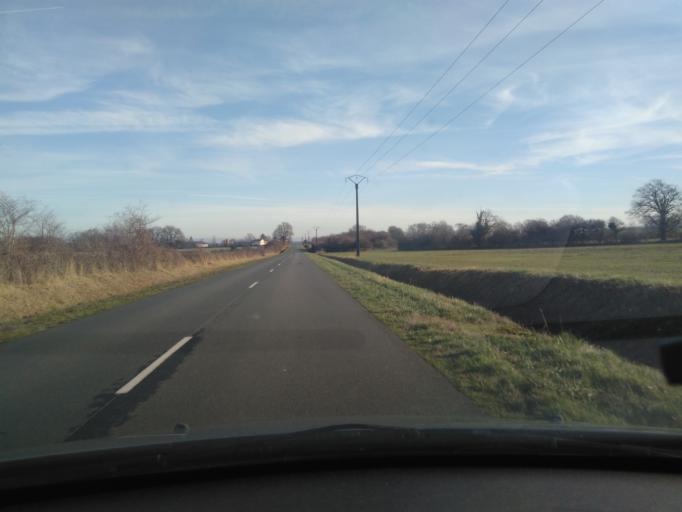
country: FR
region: Centre
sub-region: Departement du Cher
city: Le Chatelet
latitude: 46.6460
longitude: 2.3483
